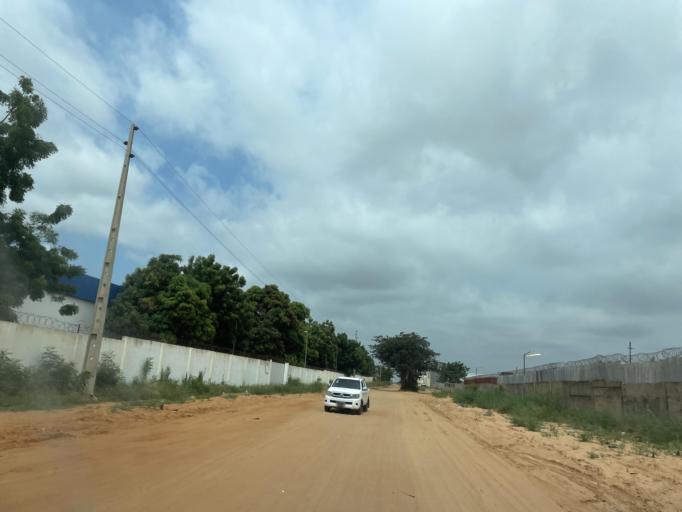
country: AO
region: Luanda
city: Luanda
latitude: -8.9336
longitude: 13.3931
